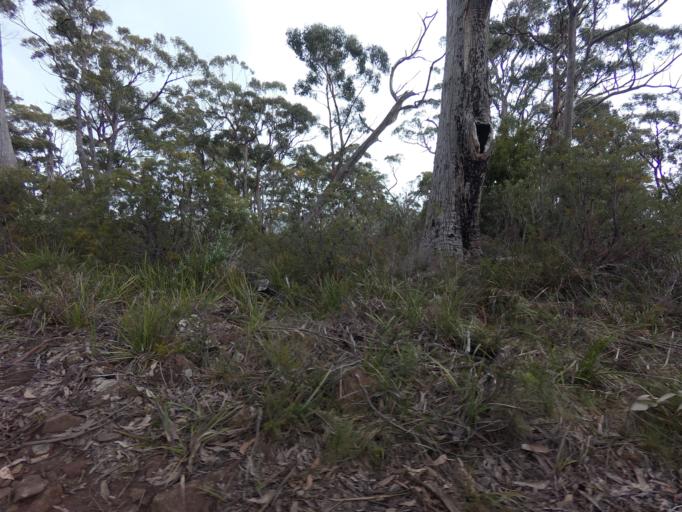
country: AU
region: Tasmania
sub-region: Huon Valley
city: Geeveston
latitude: -43.4640
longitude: 146.9184
